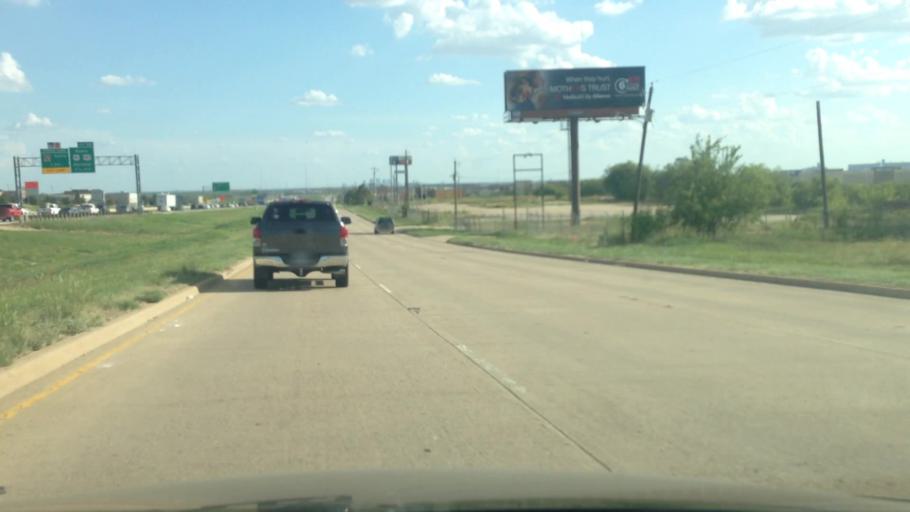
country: US
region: Texas
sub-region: Tarrant County
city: Blue Mound
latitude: 32.9109
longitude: -97.3177
